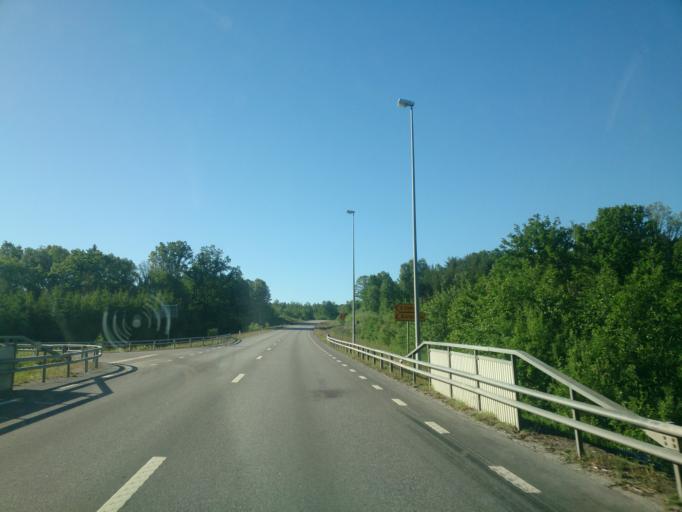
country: SE
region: OEstergoetland
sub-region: Atvidabergs Kommun
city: Atvidaberg
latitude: 58.1938
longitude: 16.0207
